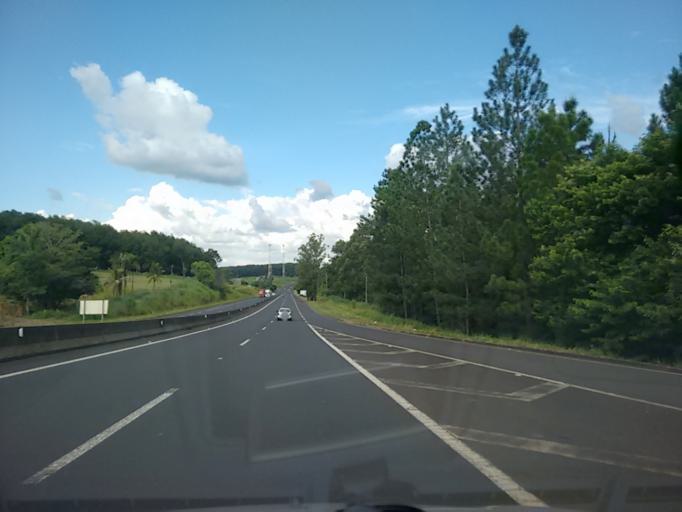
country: BR
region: Sao Paulo
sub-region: Marilia
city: Marilia
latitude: -22.2168
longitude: -49.8540
